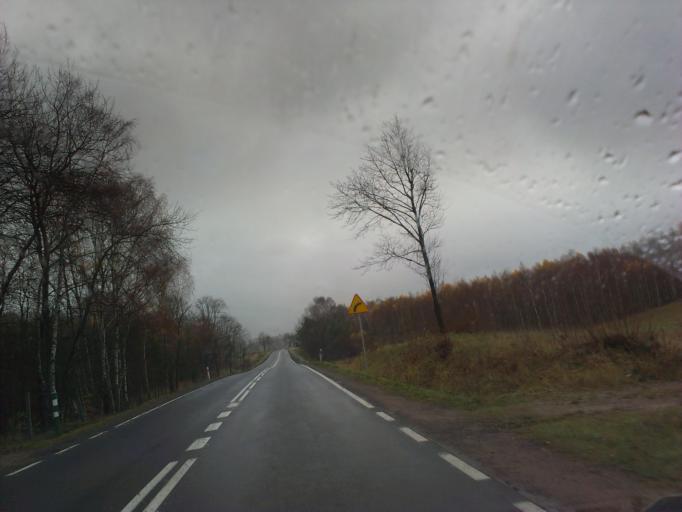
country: PL
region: West Pomeranian Voivodeship
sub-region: Powiat szczecinecki
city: Borne Sulinowo
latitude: 53.6115
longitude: 16.5573
